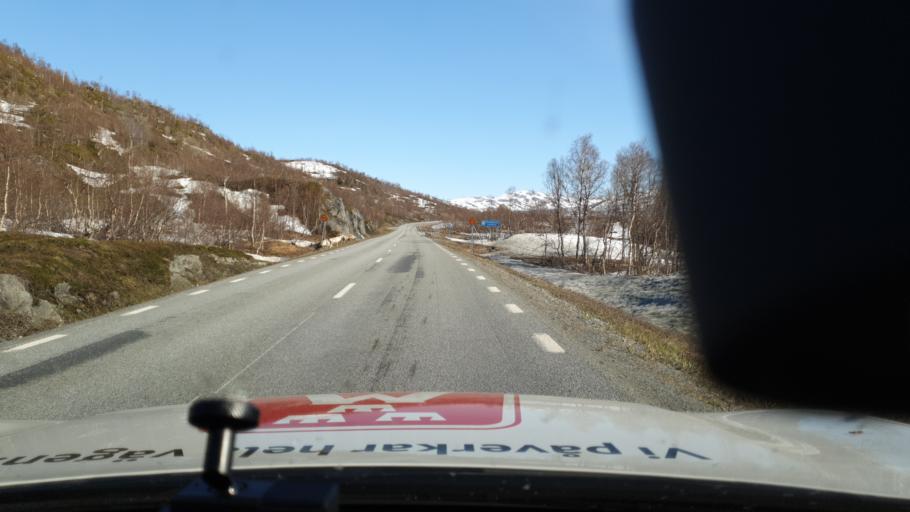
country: NO
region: Nordland
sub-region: Rana
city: Mo i Rana
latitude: 66.1332
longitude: 14.5955
